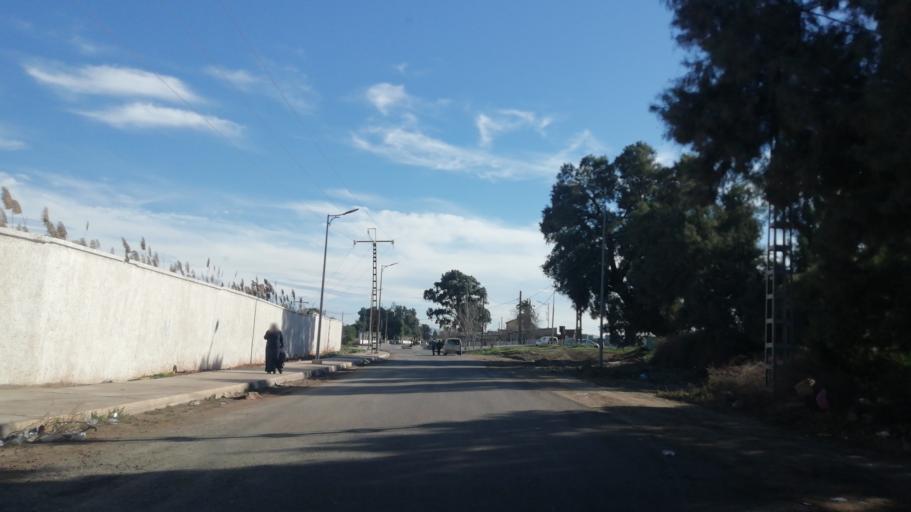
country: DZ
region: Oran
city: Es Senia
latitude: 35.6180
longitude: -0.5858
